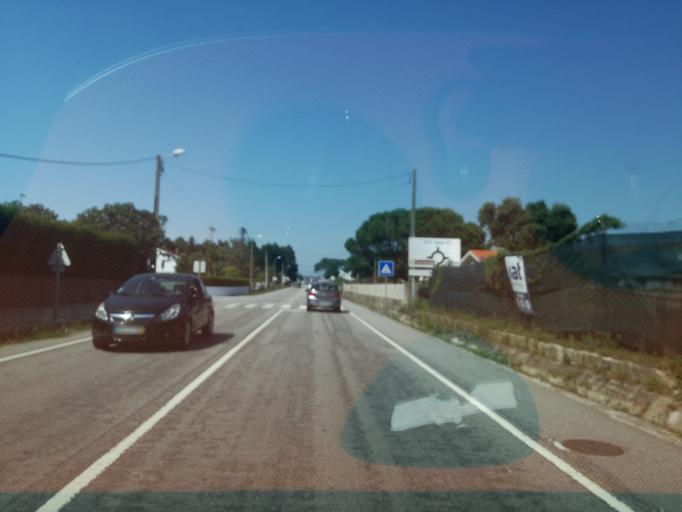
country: PT
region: Braga
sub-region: Esposende
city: Esposende
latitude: 41.5430
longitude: -8.7822
